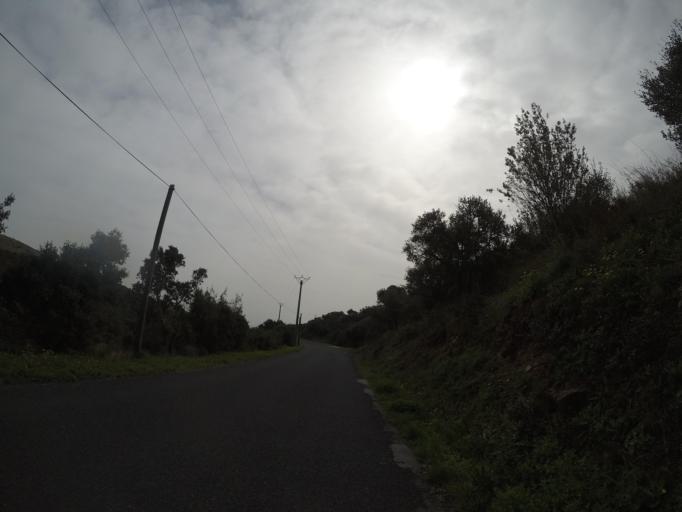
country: FR
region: Languedoc-Roussillon
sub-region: Departement des Pyrenees-Orientales
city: Corneilla-la-Riviere
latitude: 42.7314
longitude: 2.7365
